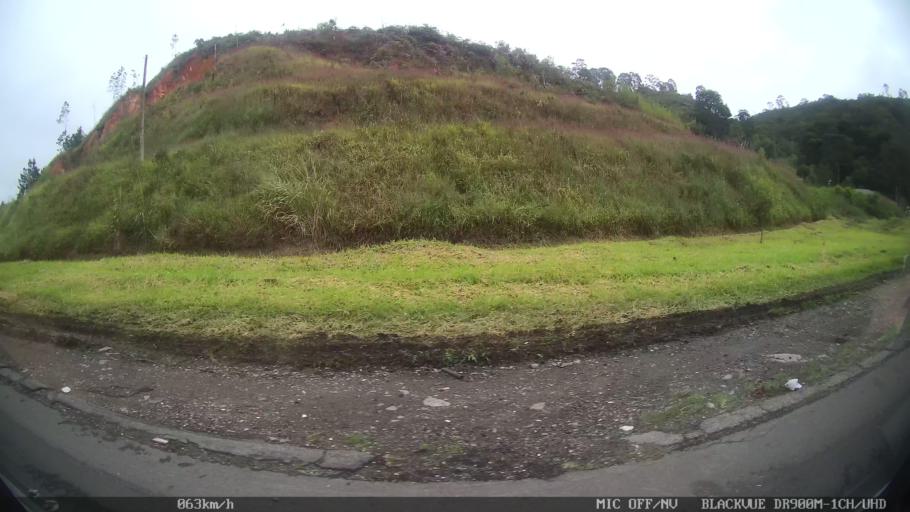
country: BR
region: Parana
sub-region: Campina Grande Do Sul
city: Campina Grande do Sul
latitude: -25.1145
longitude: -48.8469
